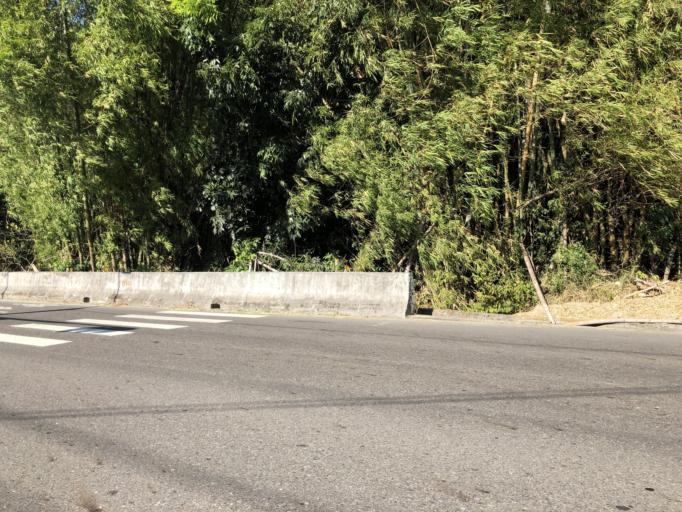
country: TW
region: Taiwan
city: Yujing
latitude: 23.0562
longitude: 120.4003
